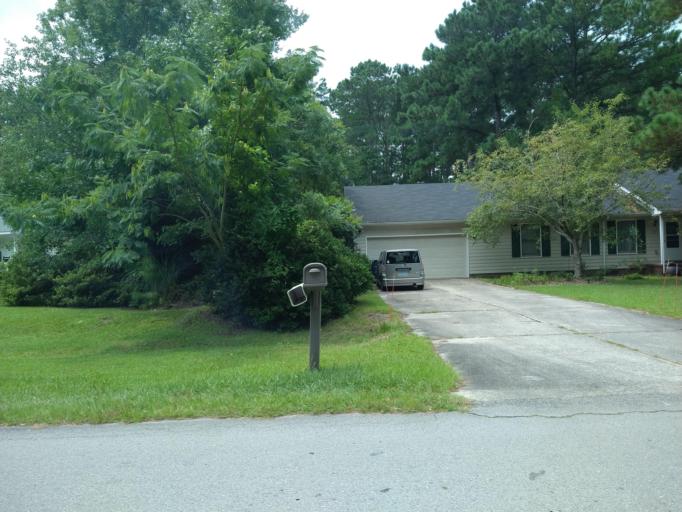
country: US
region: North Carolina
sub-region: Onslow County
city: Pumpkin Center
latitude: 34.7654
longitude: -77.3706
